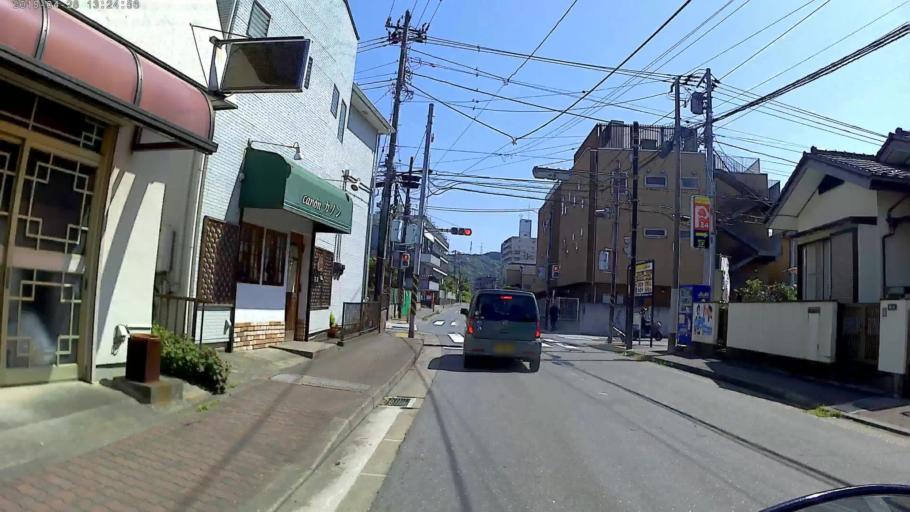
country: JP
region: Kanagawa
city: Yokosuka
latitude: 35.2317
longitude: 139.6974
